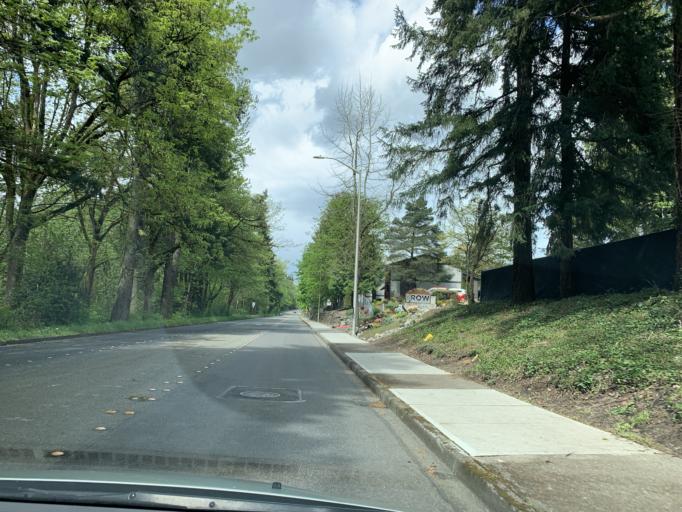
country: US
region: Washington
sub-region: King County
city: Kent
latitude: 47.3696
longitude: -122.2078
